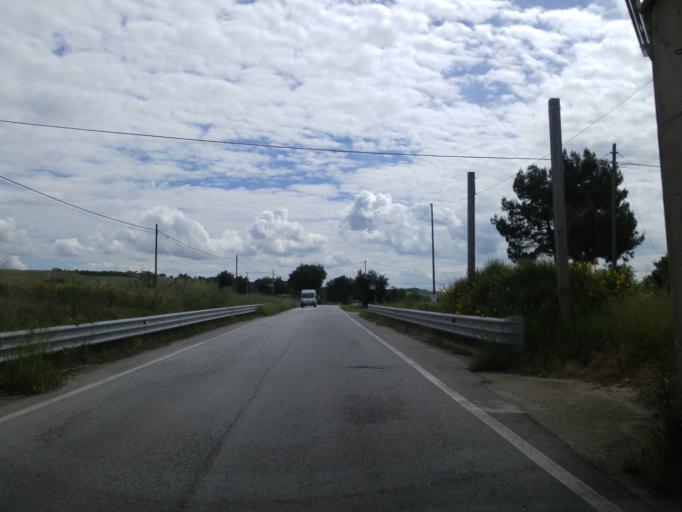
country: IT
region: The Marches
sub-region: Provincia di Pesaro e Urbino
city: Fano
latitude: 43.8095
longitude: 13.0482
